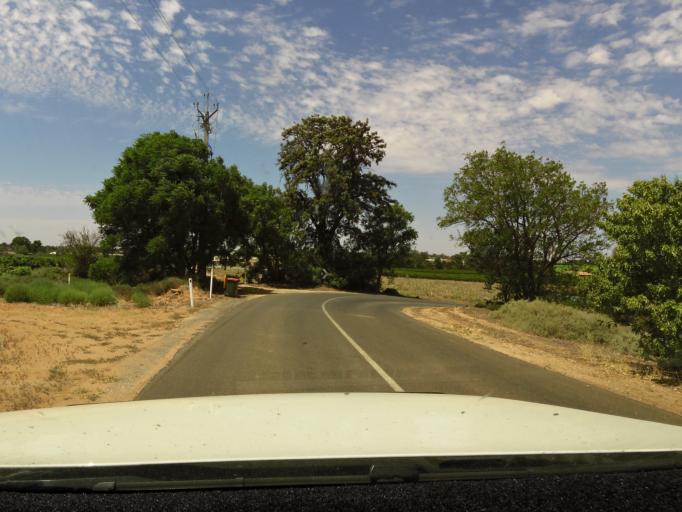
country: AU
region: South Australia
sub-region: Berri and Barmera
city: Berri
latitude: -34.2788
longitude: 140.5645
